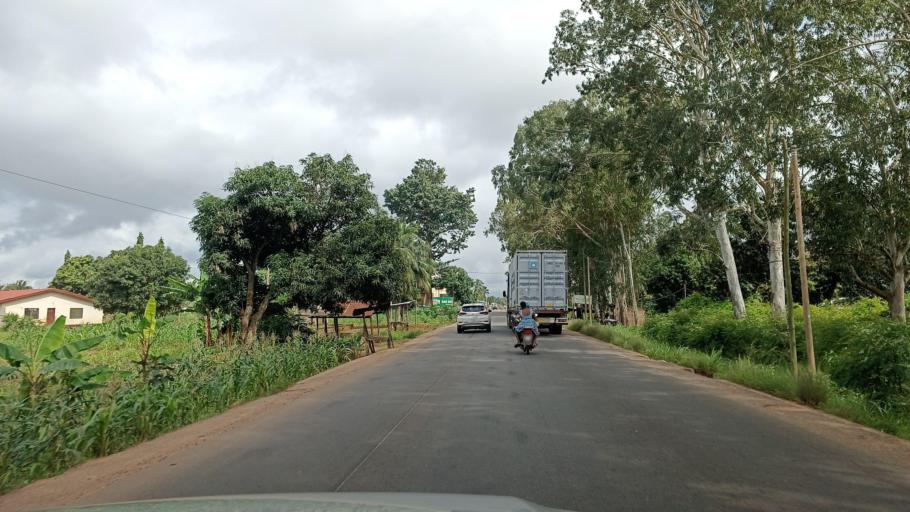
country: TG
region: Maritime
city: Tsevie
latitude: 6.3797
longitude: 1.2040
